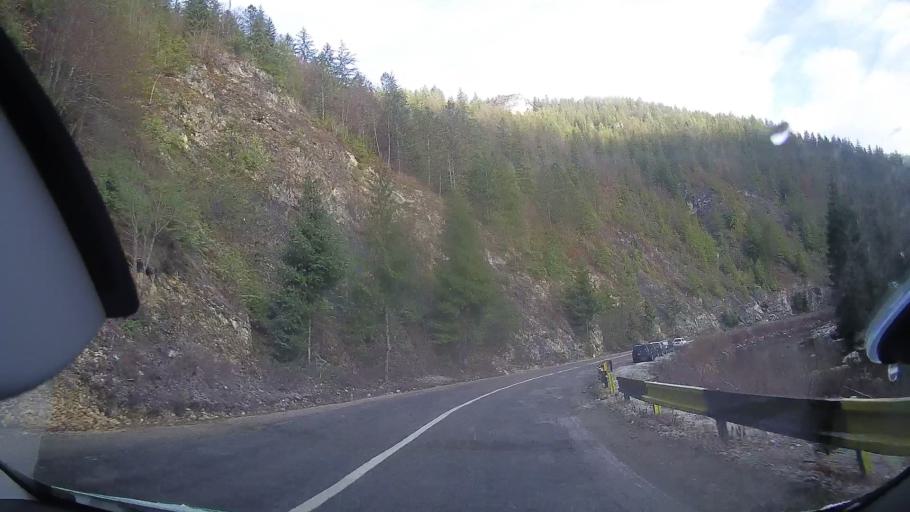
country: RO
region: Alba
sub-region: Comuna Albac
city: Albac
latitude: 46.4561
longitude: 22.9327
